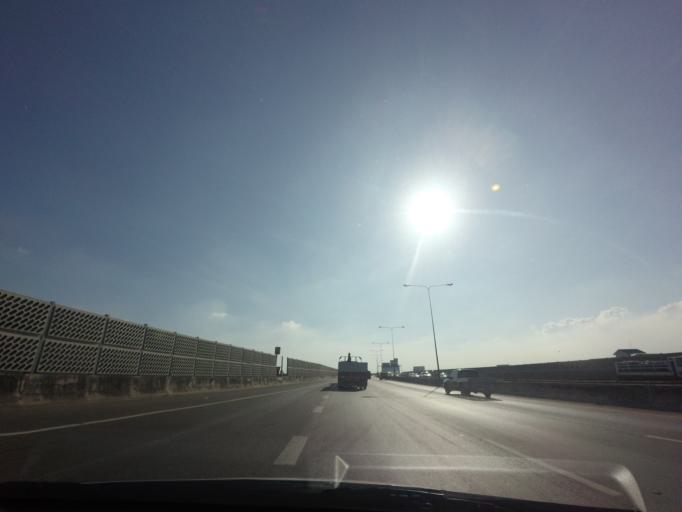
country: TH
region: Samut Prakan
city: Samut Prakan
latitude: 13.6061
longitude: 100.6555
